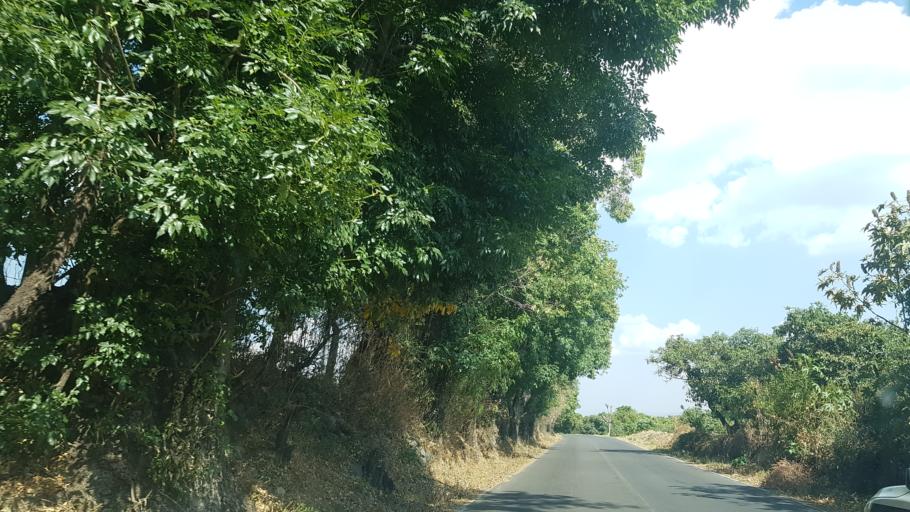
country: MX
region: Puebla
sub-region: Atlixco
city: Colonia Agricola de Ocotepec (Colonia San Jose)
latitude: 18.9217
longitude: -98.5390
